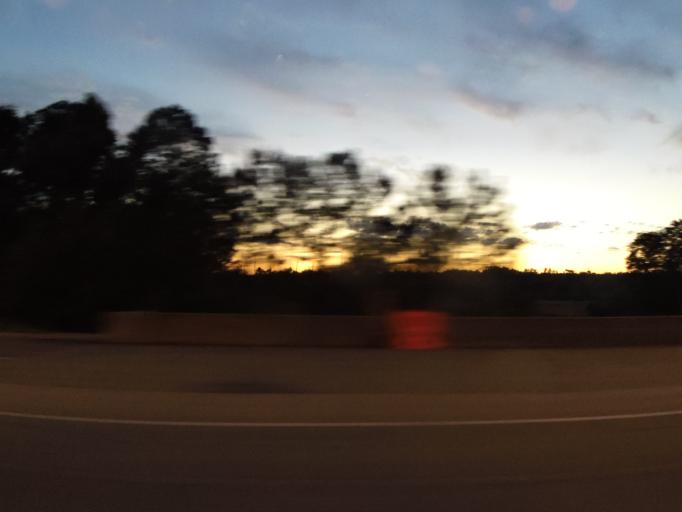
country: US
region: Georgia
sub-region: Liberty County
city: Midway
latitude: 31.6591
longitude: -81.3931
